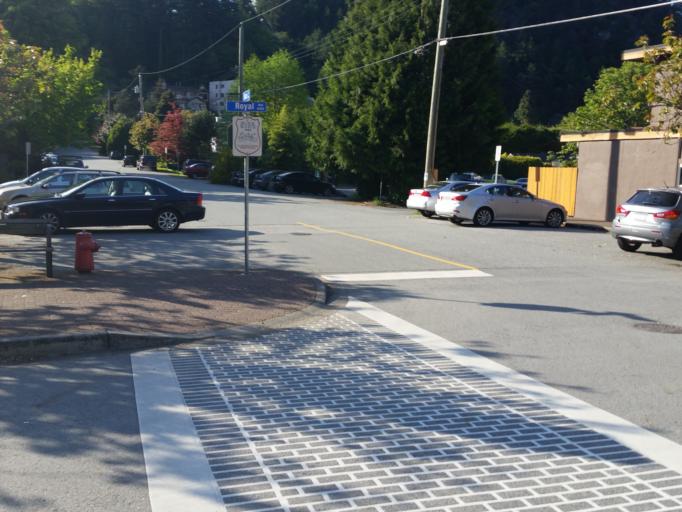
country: CA
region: British Columbia
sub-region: Greater Vancouver Regional District
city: Bowen Island
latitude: 49.3737
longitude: -123.2751
